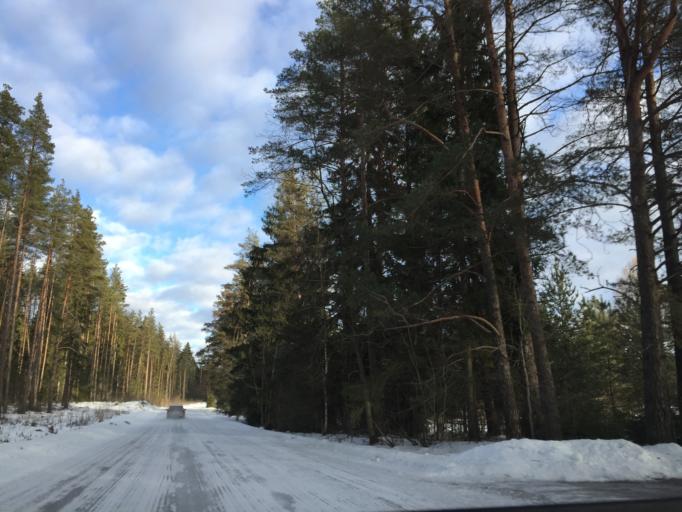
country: LV
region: Ogre
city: Jumprava
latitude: 56.5665
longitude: 24.9260
